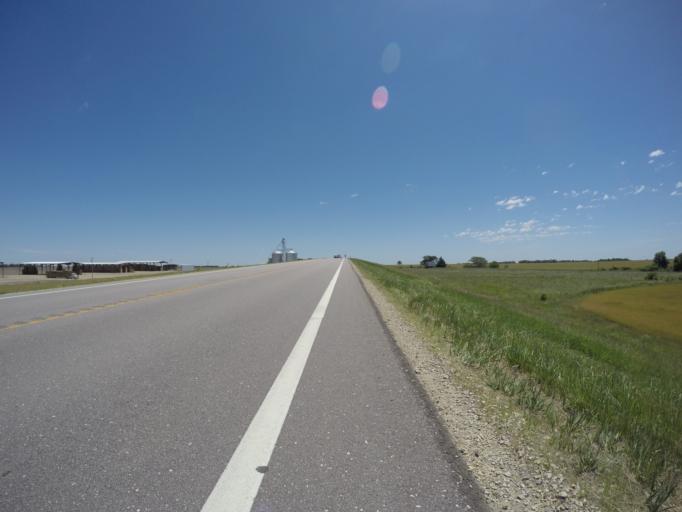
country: US
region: Kansas
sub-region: Republic County
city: Belleville
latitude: 39.8123
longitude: -97.7170
